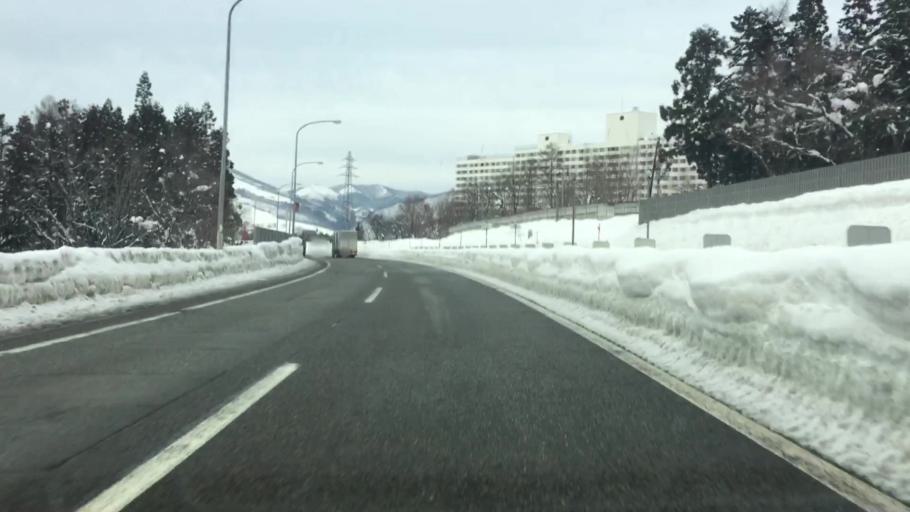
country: JP
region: Niigata
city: Shiozawa
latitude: 36.9016
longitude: 138.8476
